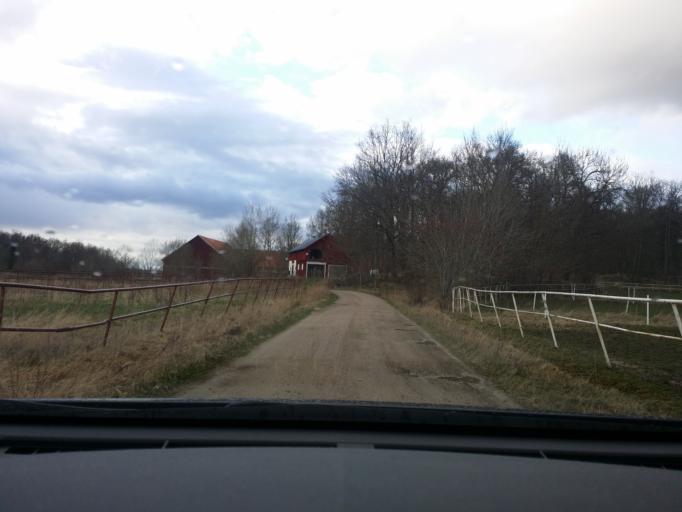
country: SE
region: Soedermanland
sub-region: Eskilstuna Kommun
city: Arla
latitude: 59.3790
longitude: 16.6483
